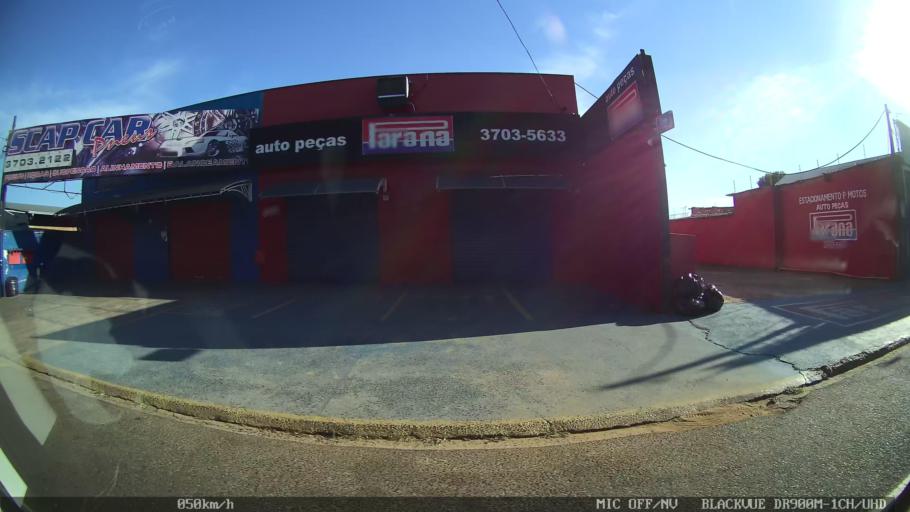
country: BR
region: Sao Paulo
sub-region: Franca
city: Franca
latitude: -20.5072
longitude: -47.4025
